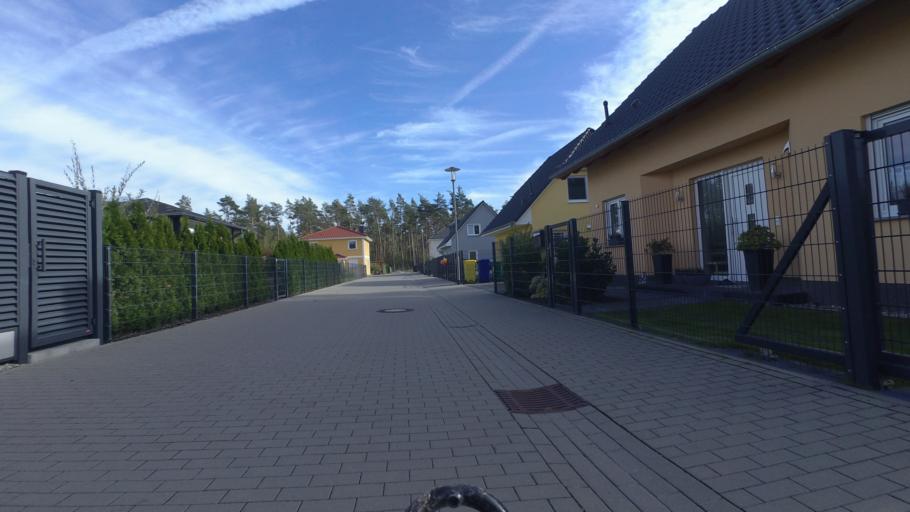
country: DE
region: Brandenburg
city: Ludwigsfelde
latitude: 52.3066
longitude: 13.2233
